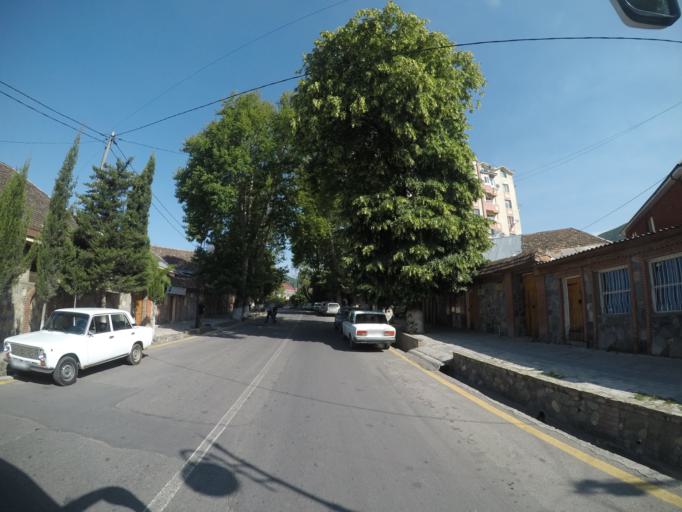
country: AZ
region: Shaki City
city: Sheki
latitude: 41.2047
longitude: 47.1779
